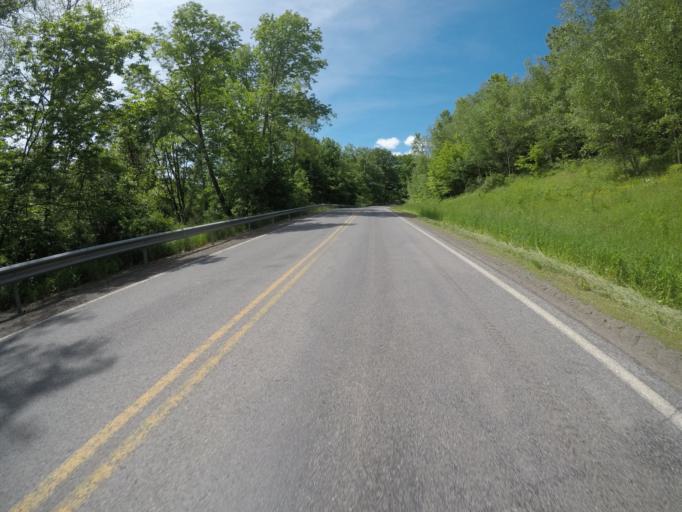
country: US
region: New York
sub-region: Delaware County
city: Delhi
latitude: 42.1606
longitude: -74.7970
